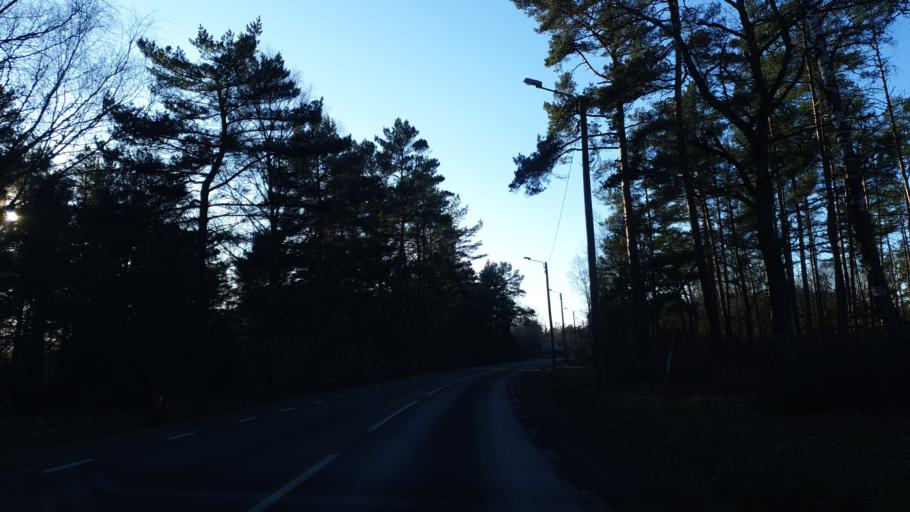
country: SE
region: Blekinge
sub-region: Karlskrona Kommun
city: Nattraby
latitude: 56.2212
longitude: 15.4051
